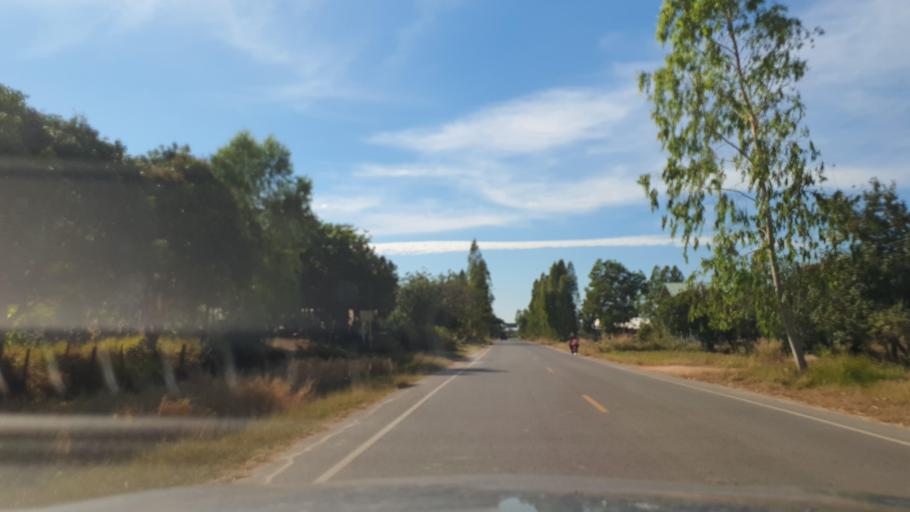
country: TH
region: Kalasin
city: Khao Wong
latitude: 16.6500
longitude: 104.1516
